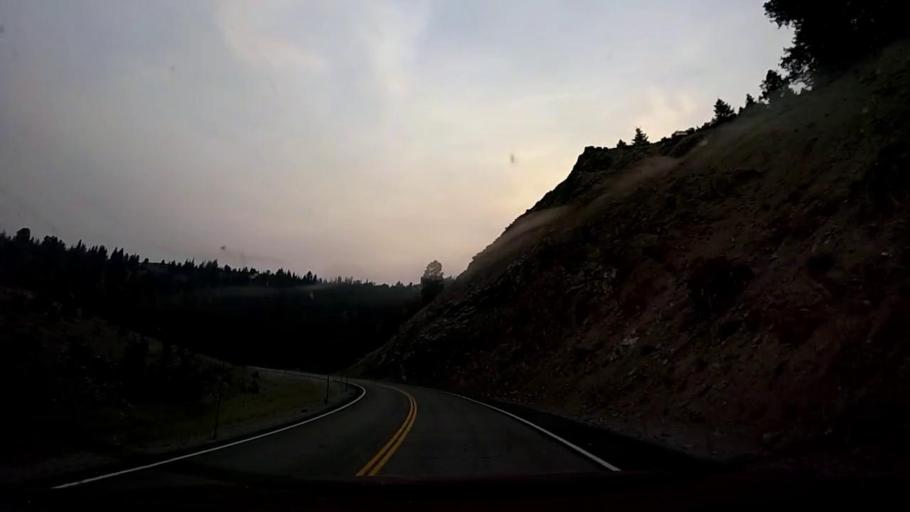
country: US
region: Idaho
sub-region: Blaine County
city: Ketchum
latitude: 43.8871
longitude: -114.6958
